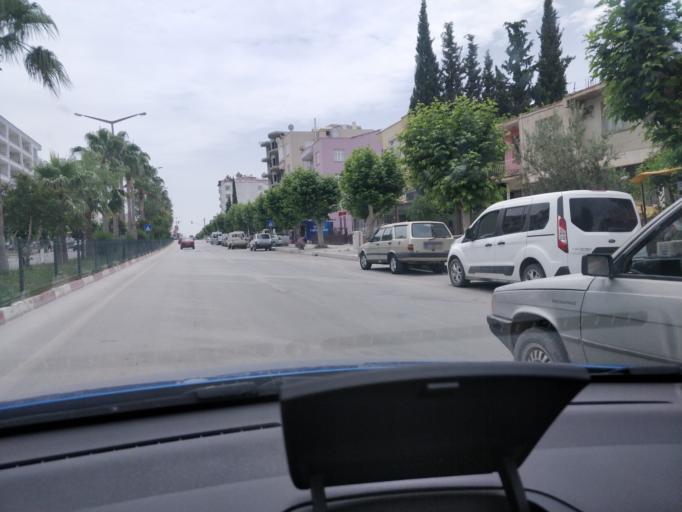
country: TR
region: Mersin
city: Mut
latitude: 36.6393
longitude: 33.4430
